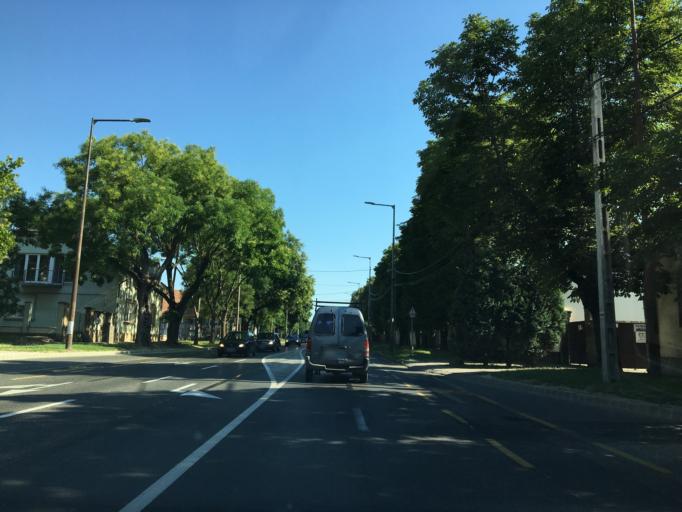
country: HU
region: Tolna
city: Szekszard
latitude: 46.3594
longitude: 18.7042
